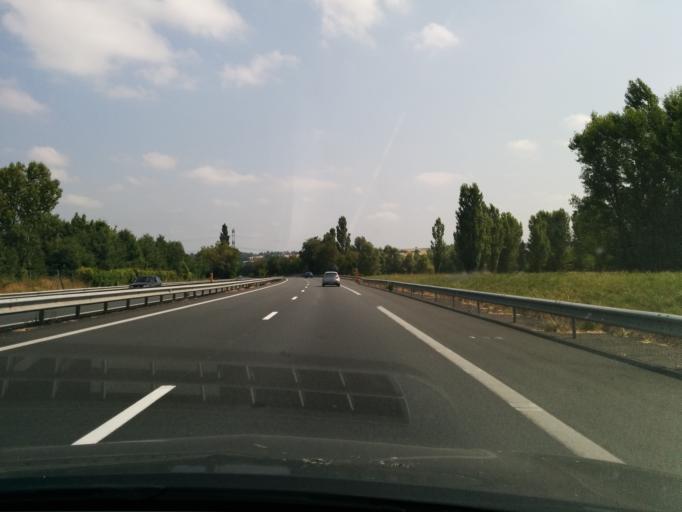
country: FR
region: Midi-Pyrenees
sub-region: Departement de la Haute-Garonne
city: Gragnague
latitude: 43.6877
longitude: 1.5655
